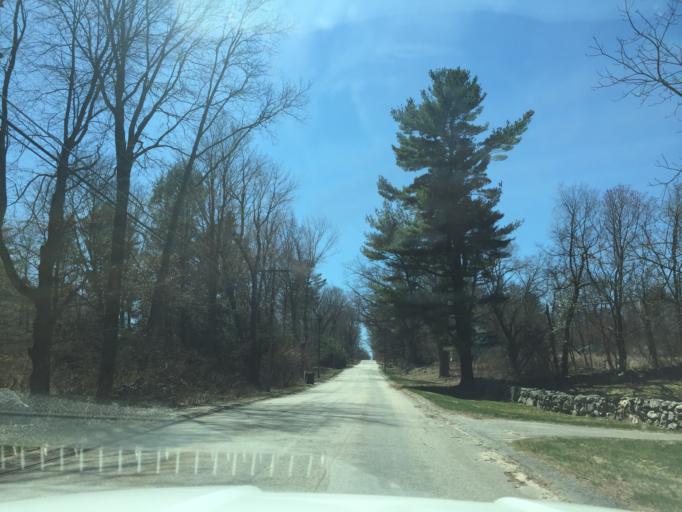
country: US
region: Connecticut
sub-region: Windham County
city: South Woodstock
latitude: 41.9602
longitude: -71.9688
